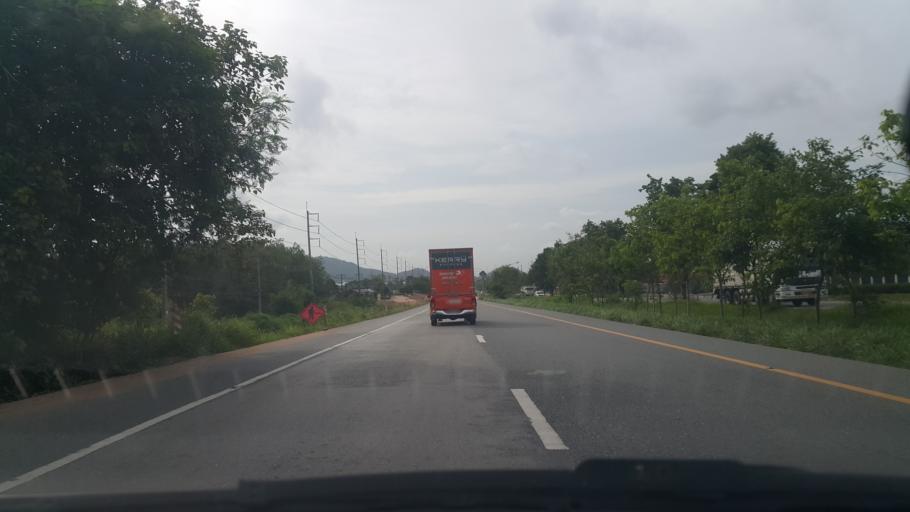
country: TH
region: Rayong
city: Nikhom Phattana
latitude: 12.7910
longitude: 101.1547
